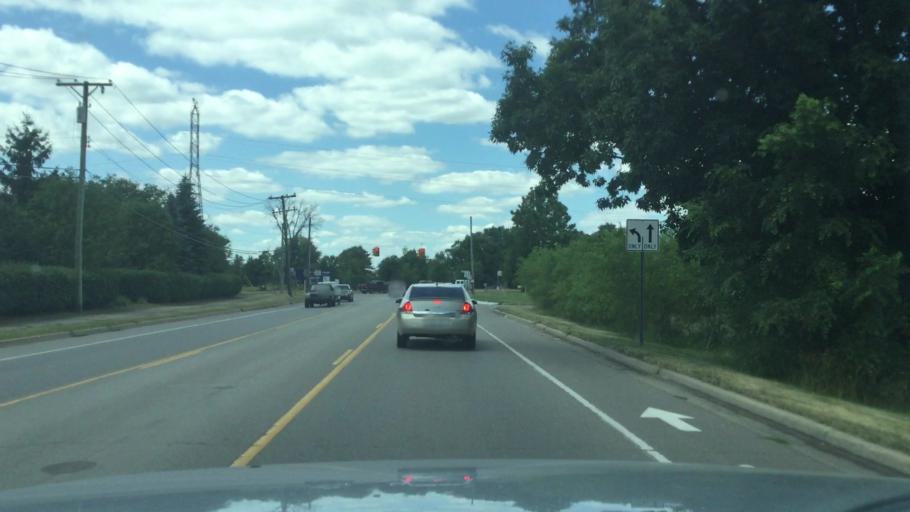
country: US
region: Michigan
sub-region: Washtenaw County
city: Ypsilanti
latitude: 42.2137
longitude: -83.5564
